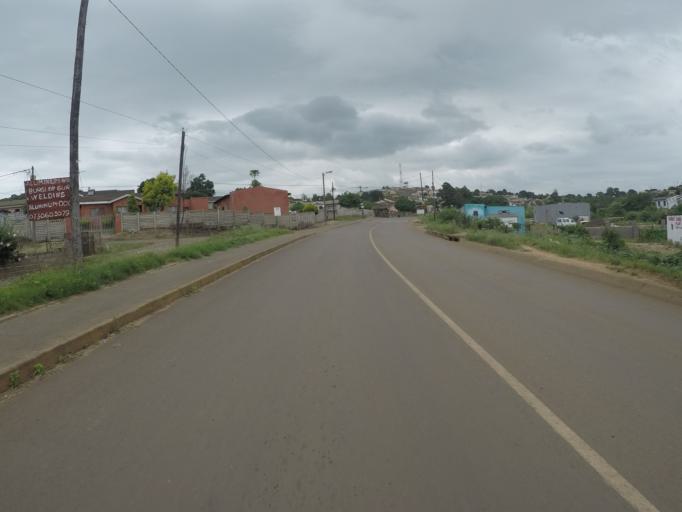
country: ZA
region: KwaZulu-Natal
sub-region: uThungulu District Municipality
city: Empangeni
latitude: -28.7822
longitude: 31.8623
